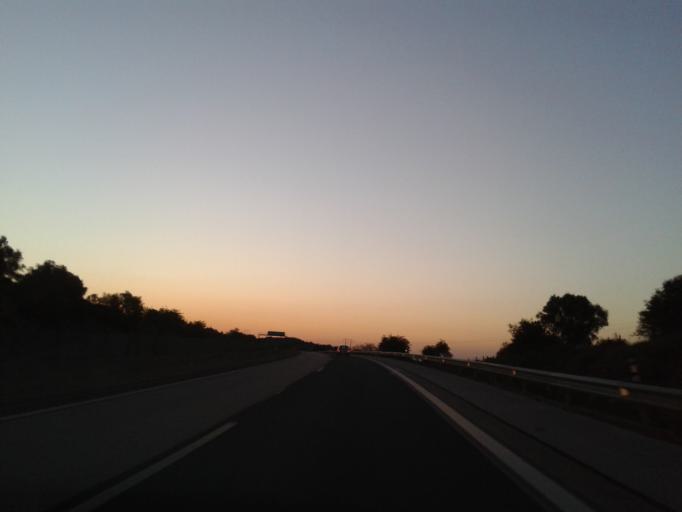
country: PT
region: Faro
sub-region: Loule
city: Boliqueime
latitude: 37.1544
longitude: -8.1768
